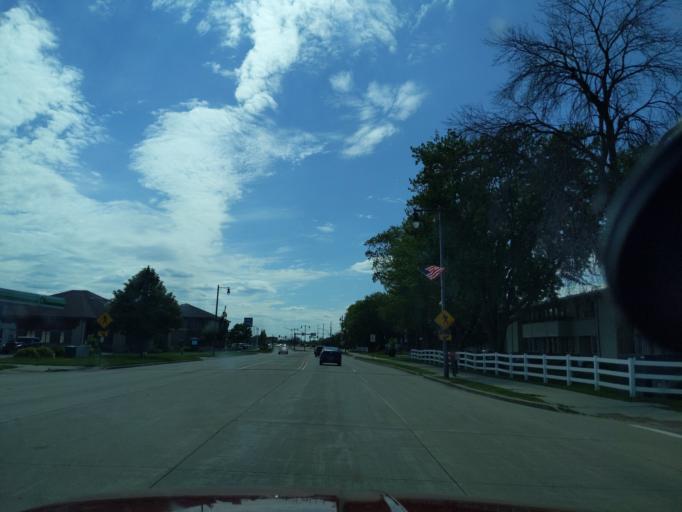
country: US
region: Wisconsin
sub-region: Dane County
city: Sun Prairie
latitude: 43.1778
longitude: -89.2416
